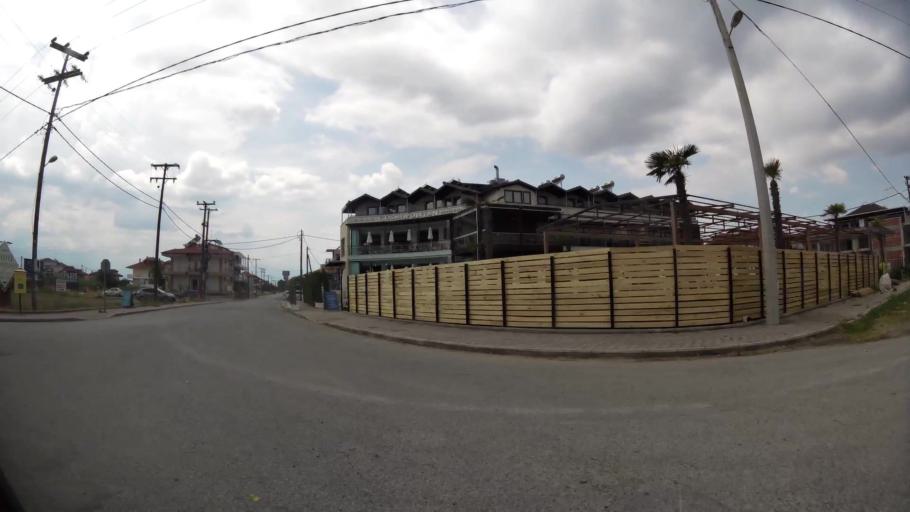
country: GR
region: Central Macedonia
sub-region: Nomos Pierias
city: Paralia
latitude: 40.2760
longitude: 22.5969
